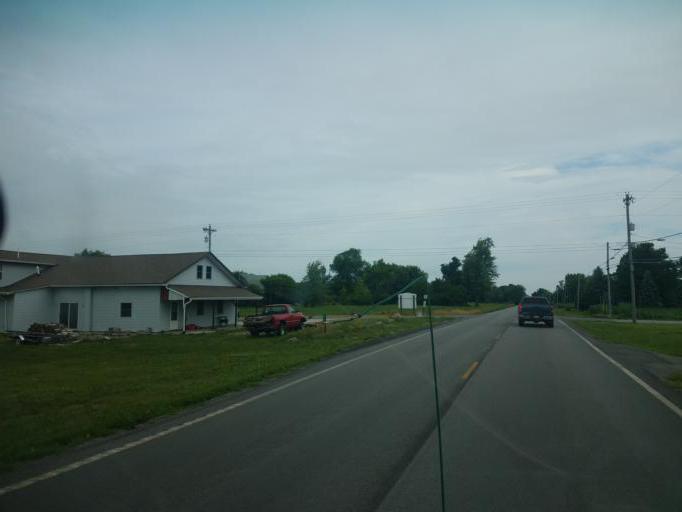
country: US
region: Ohio
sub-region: Hardin County
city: Ada
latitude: 40.7907
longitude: -83.8232
